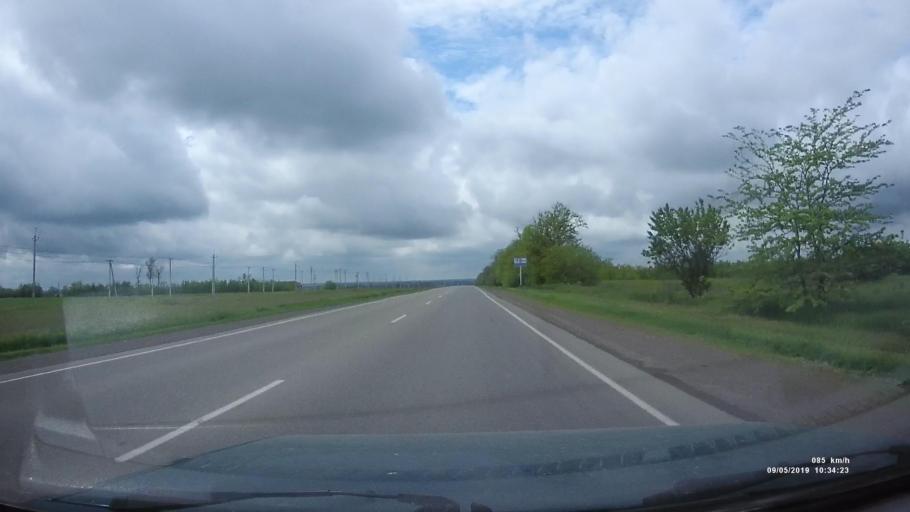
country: RU
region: Rostov
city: Peshkovo
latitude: 47.0548
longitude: 39.4201
